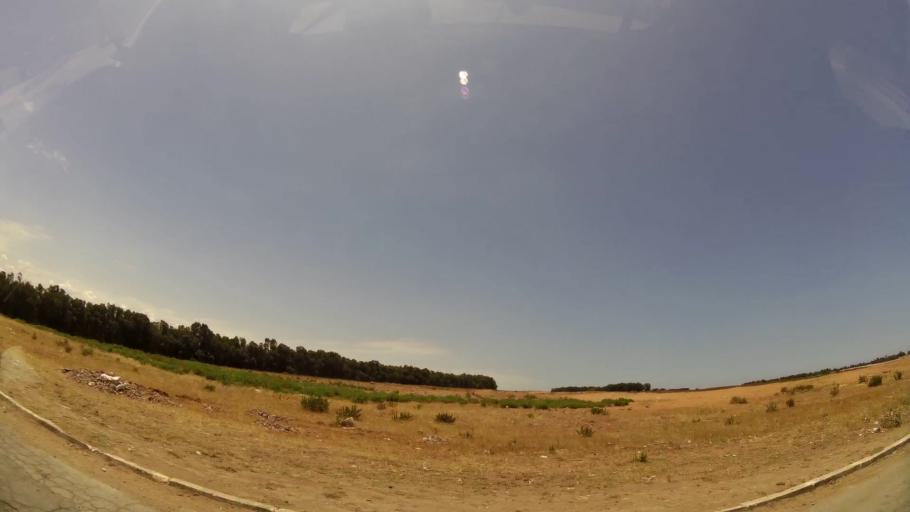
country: MA
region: Gharb-Chrarda-Beni Hssen
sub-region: Kenitra Province
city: Kenitra
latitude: 34.2488
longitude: -6.6239
